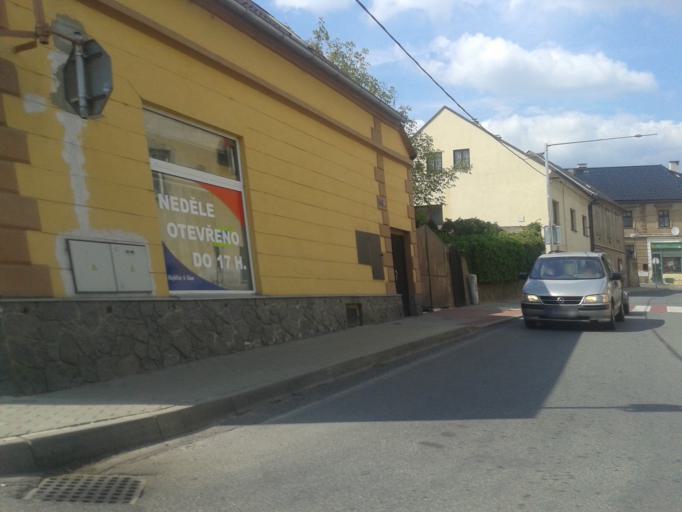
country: CZ
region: Central Bohemia
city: Zdice
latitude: 49.9139
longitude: 13.9797
